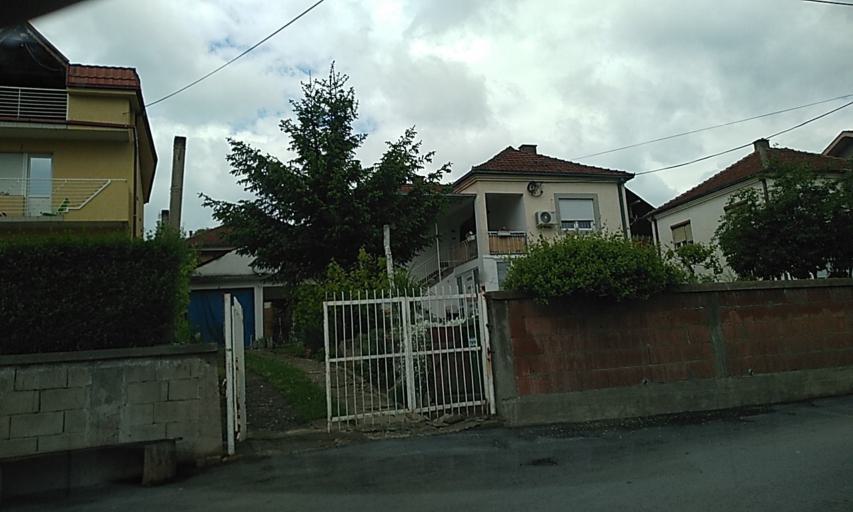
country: RS
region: Central Serbia
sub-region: Pcinjski Okrug
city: Vladicin Han
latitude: 42.7139
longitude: 22.0617
